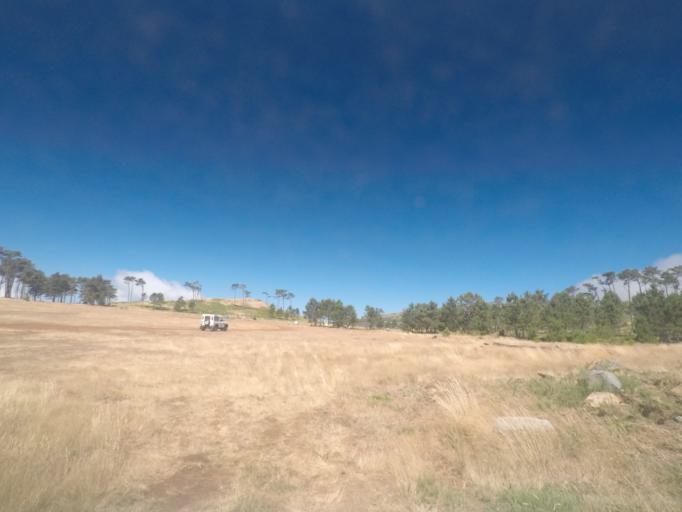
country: PT
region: Madeira
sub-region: Funchal
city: Nossa Senhora do Monte
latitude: 32.7117
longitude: -16.9099
